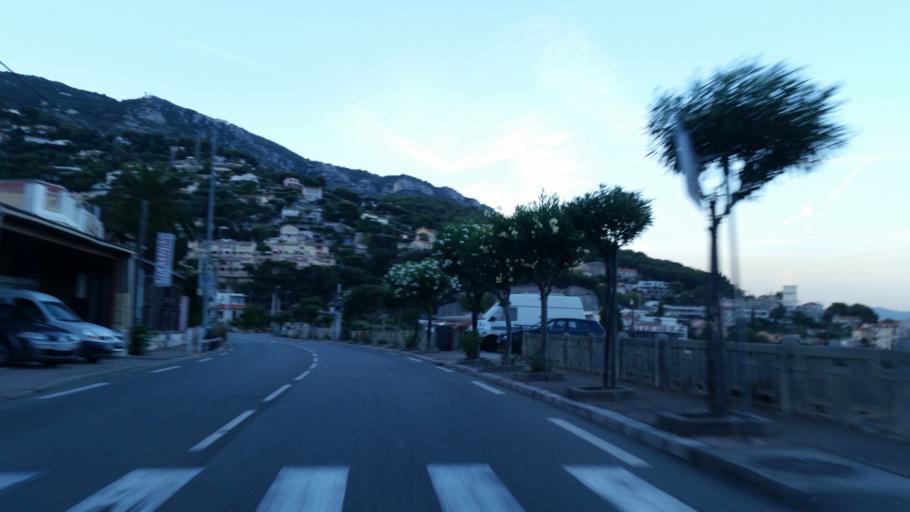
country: MC
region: Commune de Monaco
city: Moneghetti
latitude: 43.7393
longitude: 7.4127
